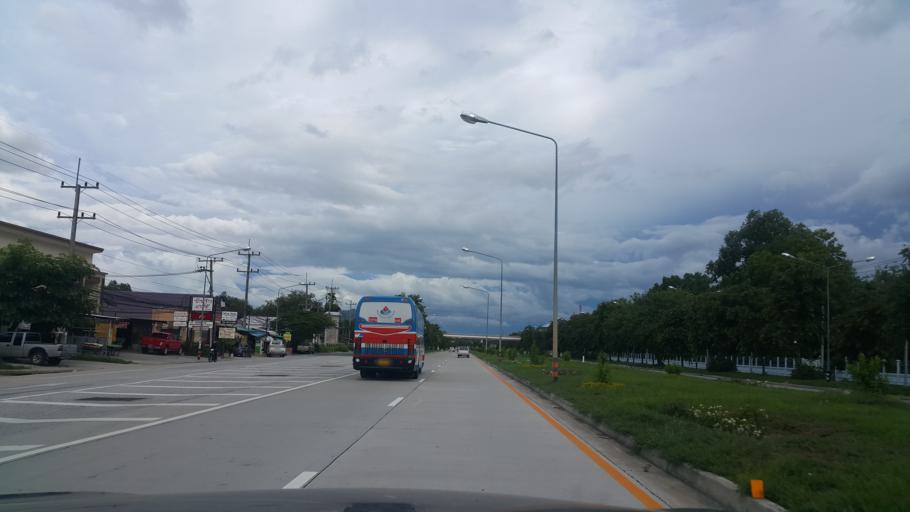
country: TH
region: Tak
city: Tak
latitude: 16.9059
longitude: 99.1235
